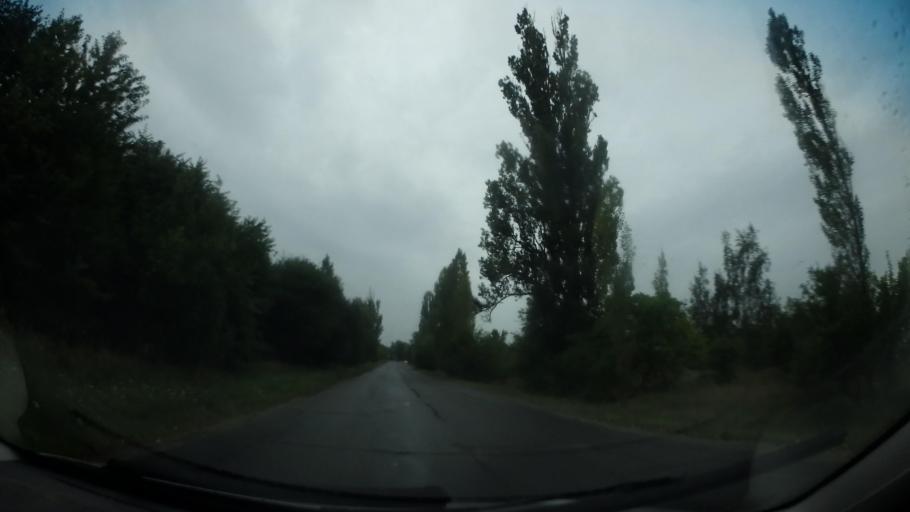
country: CZ
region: Central Bohemia
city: Milovice
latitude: 50.2338
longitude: 14.8966
